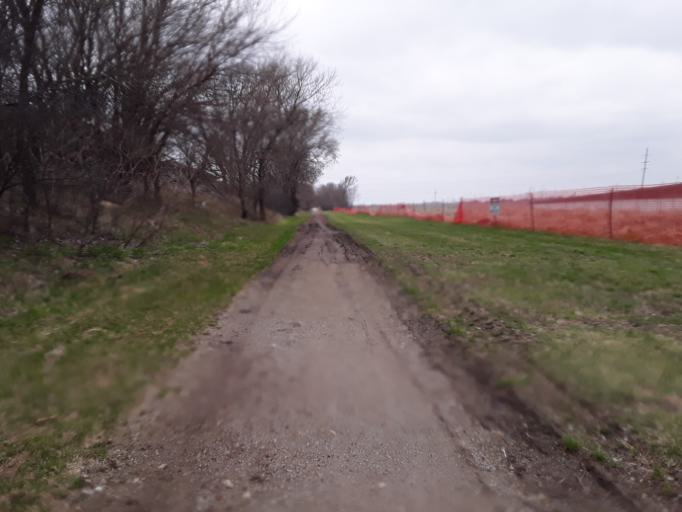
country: US
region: Nebraska
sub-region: Lancaster County
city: Lincoln
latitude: 40.8513
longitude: -96.6010
